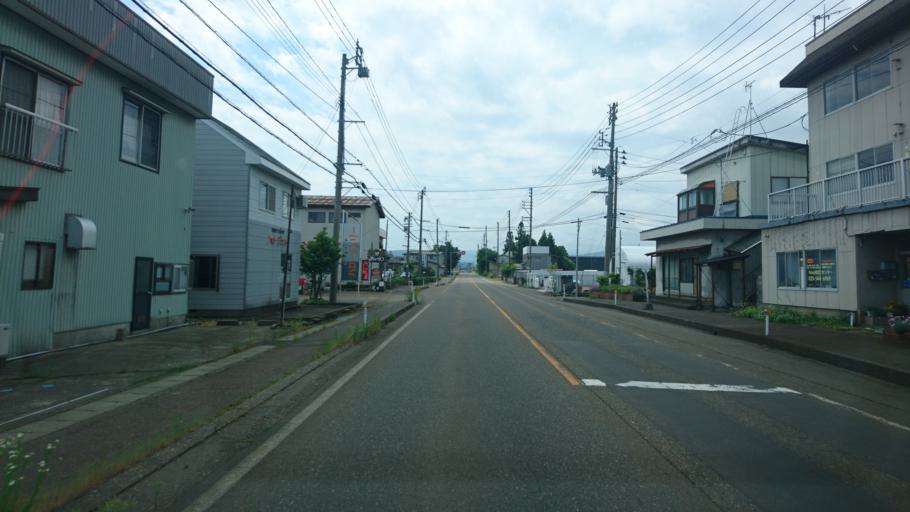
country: JP
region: Niigata
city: Arai
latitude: 37.0701
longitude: 138.2572
